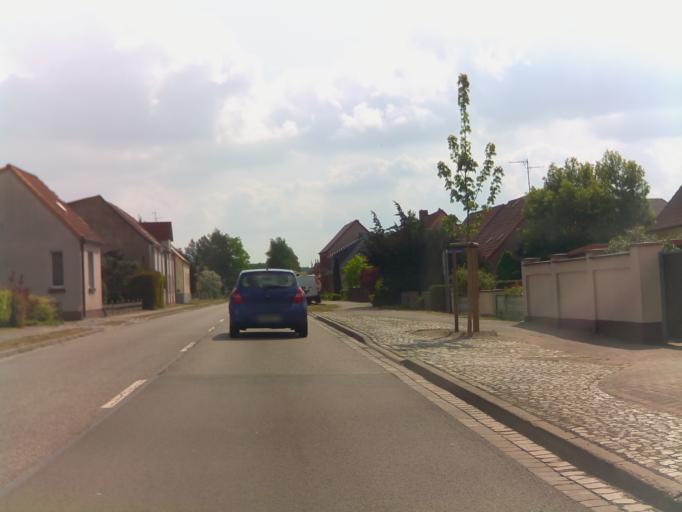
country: DE
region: Saxony-Anhalt
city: Javenitz
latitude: 52.5253
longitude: 11.4637
